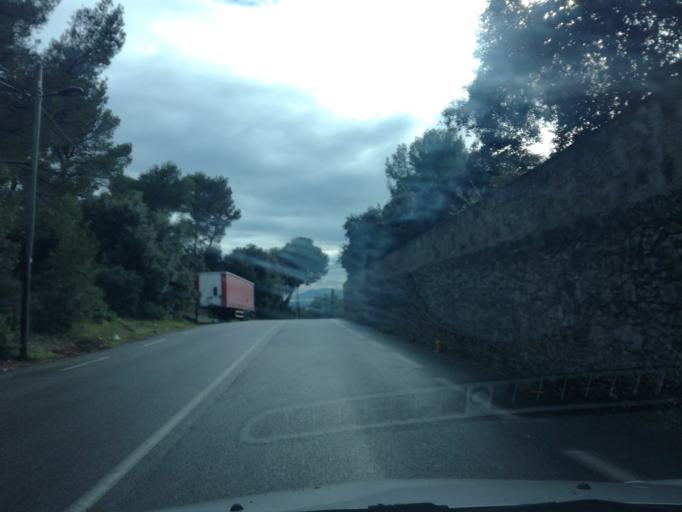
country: FR
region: Provence-Alpes-Cote d'Azur
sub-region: Departement des Alpes-Maritimes
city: Pegomas
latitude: 43.6253
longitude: 6.9350
